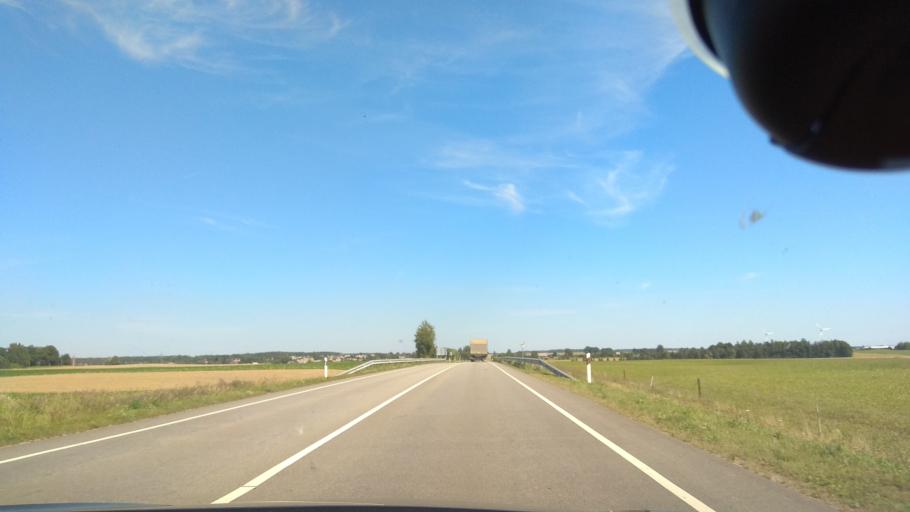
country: LT
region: Telsiu apskritis
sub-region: Telsiai
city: Telsiai
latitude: 56.0044
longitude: 22.3428
